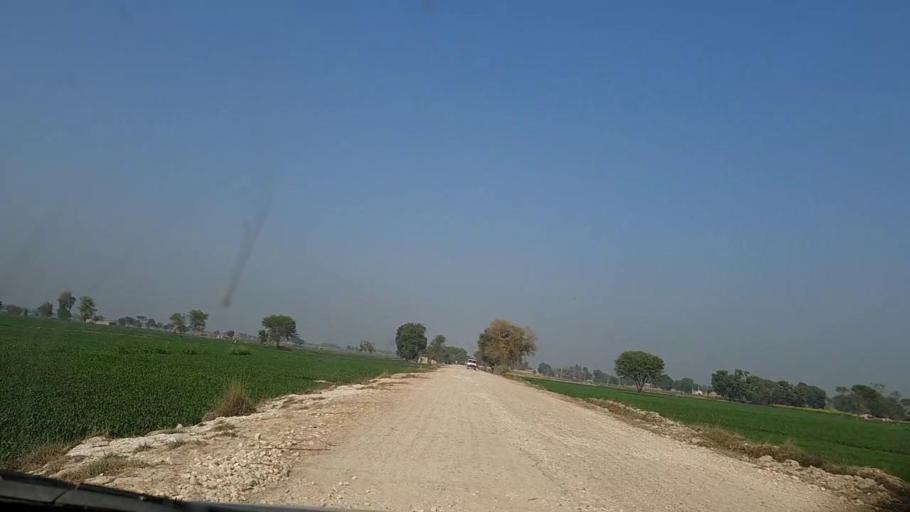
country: PK
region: Sindh
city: Moro
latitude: 26.7729
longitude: 67.9325
